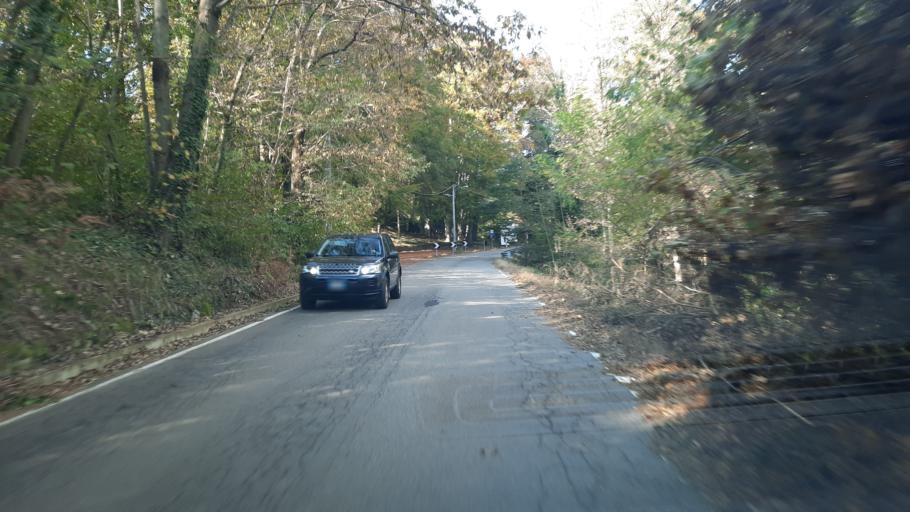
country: IT
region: Piedmont
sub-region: Provincia di Novara
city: Ameno
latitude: 45.7838
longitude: 8.4315
